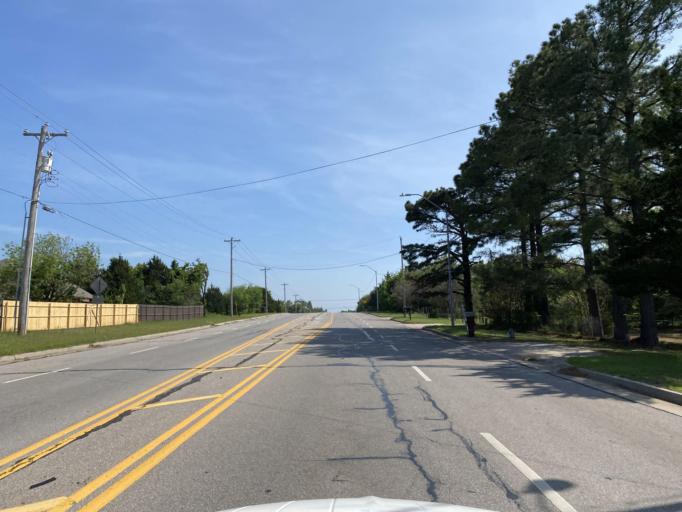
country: US
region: Oklahoma
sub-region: Oklahoma County
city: Nicoma Park
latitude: 35.4663
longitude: -97.3357
